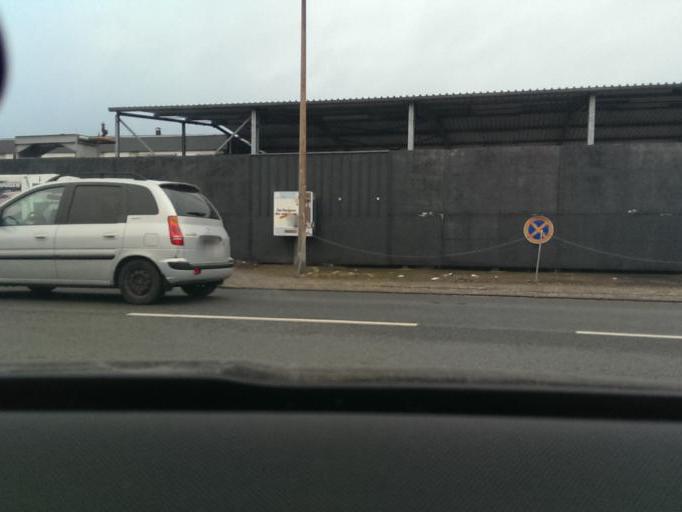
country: DE
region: Lower Saxony
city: Isernhagen Farster Bauerschaft
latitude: 52.4275
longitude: 9.8432
